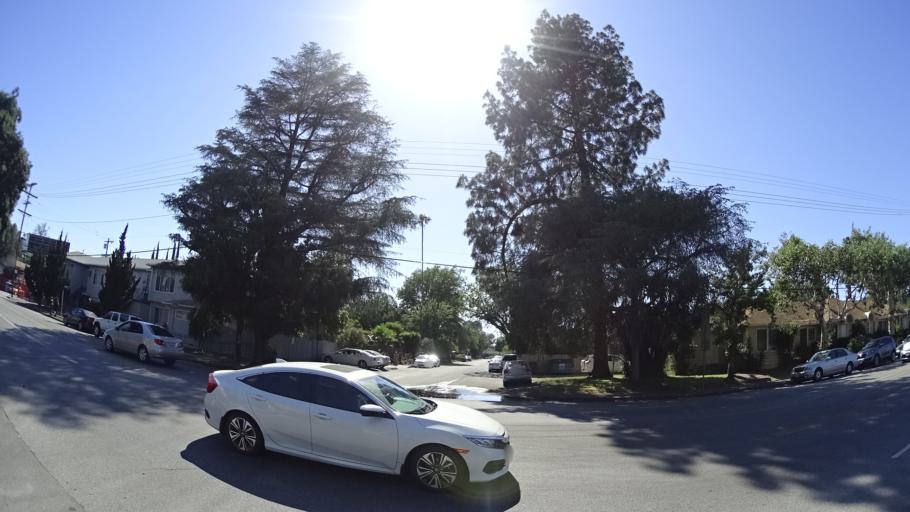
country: US
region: California
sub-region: Los Angeles County
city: North Hollywood
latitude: 34.1587
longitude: -118.3877
